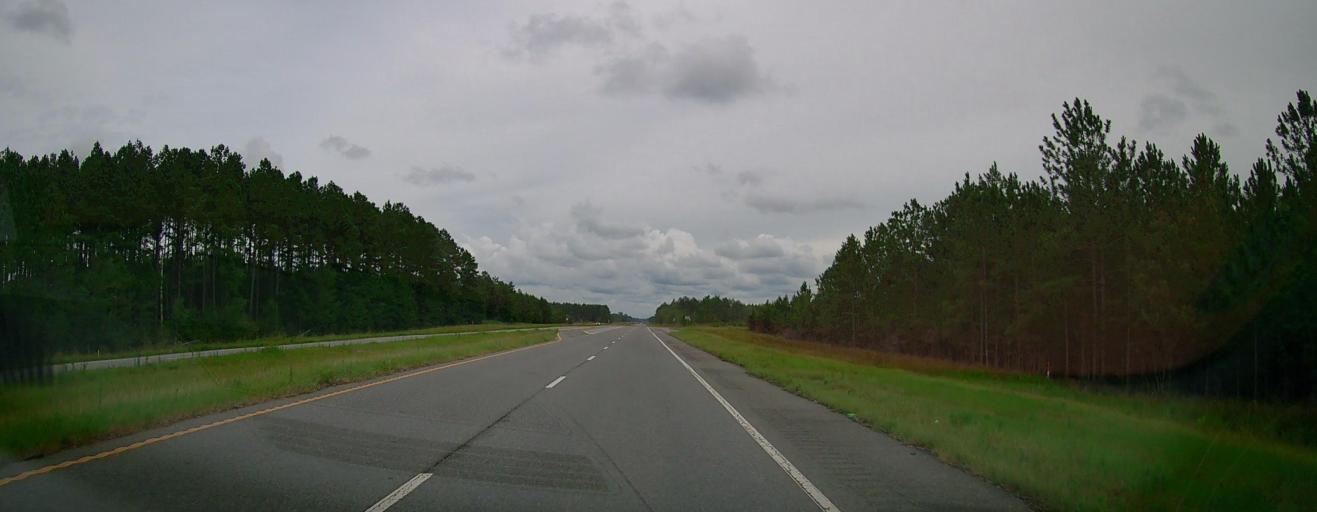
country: US
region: Georgia
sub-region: Appling County
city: Baxley
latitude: 31.7452
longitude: -82.2529
